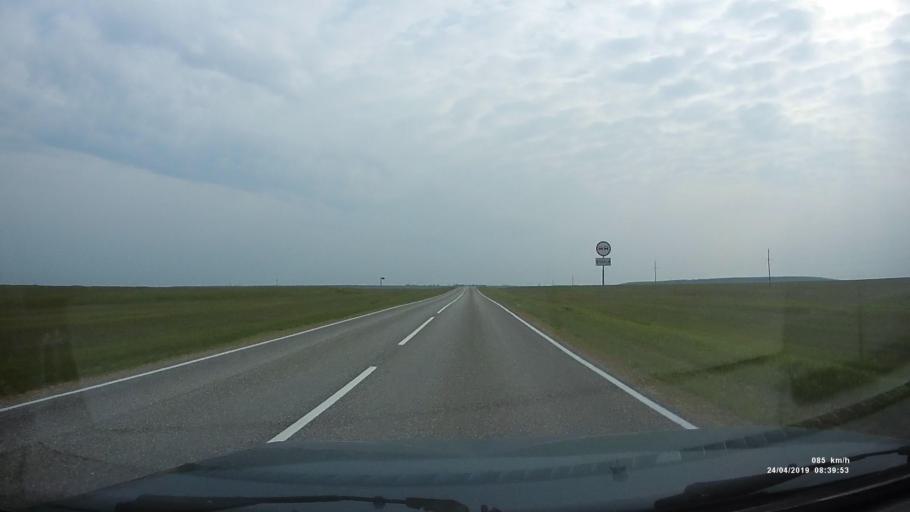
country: RU
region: Kalmykiya
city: Arshan'
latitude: 46.2234
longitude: 43.9917
